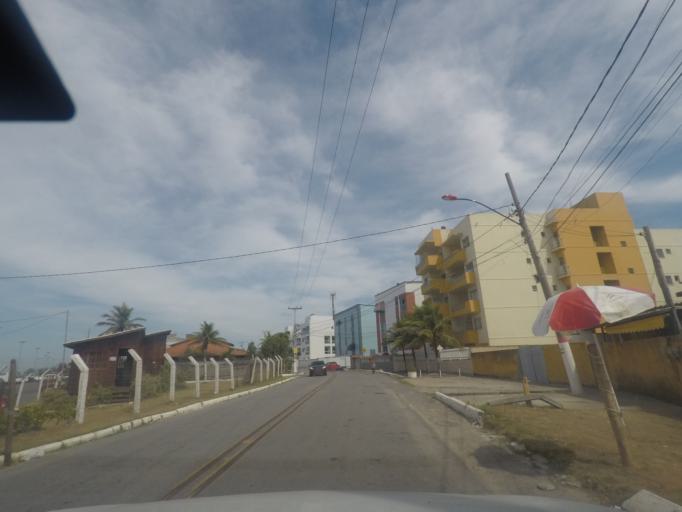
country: BR
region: Rio de Janeiro
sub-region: Marica
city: Marica
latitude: -22.9568
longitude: -42.6961
